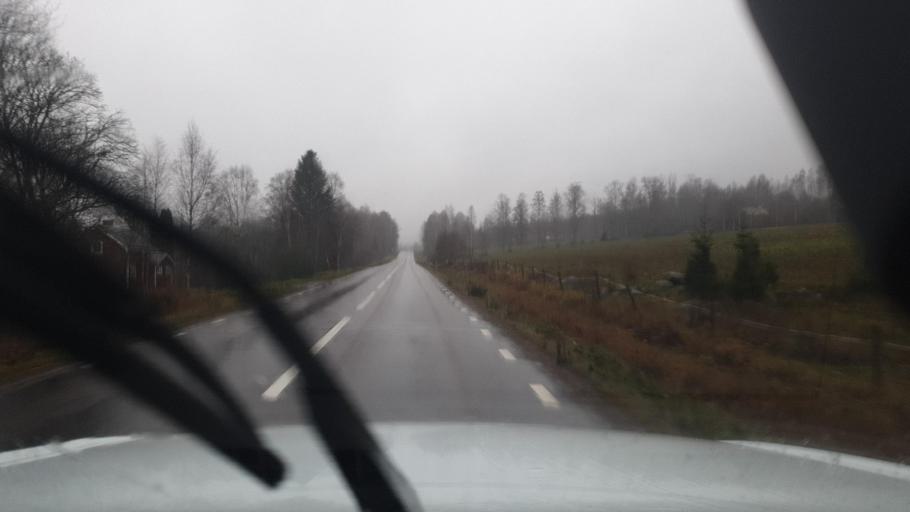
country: SE
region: Vaermland
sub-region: Torsby Kommun
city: Torsby
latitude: 59.9374
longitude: 12.9010
